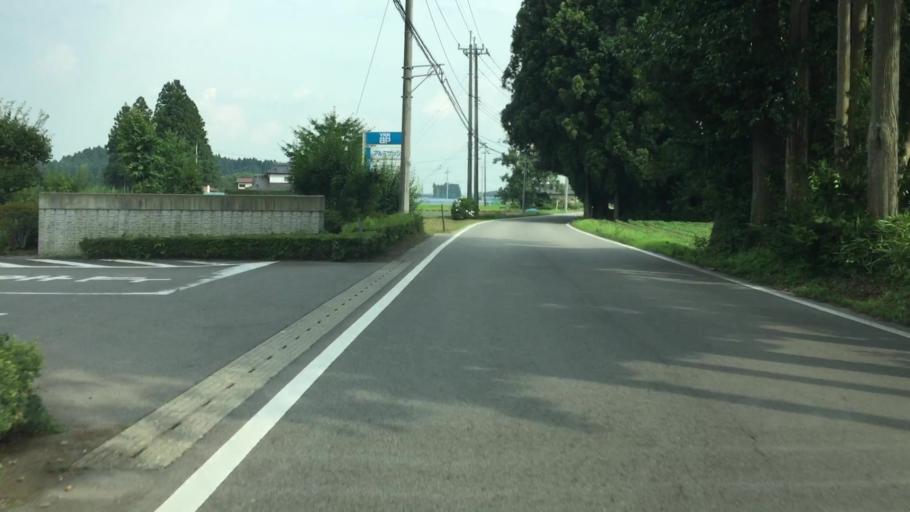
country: JP
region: Tochigi
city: Kuroiso
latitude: 36.9675
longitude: 139.9789
